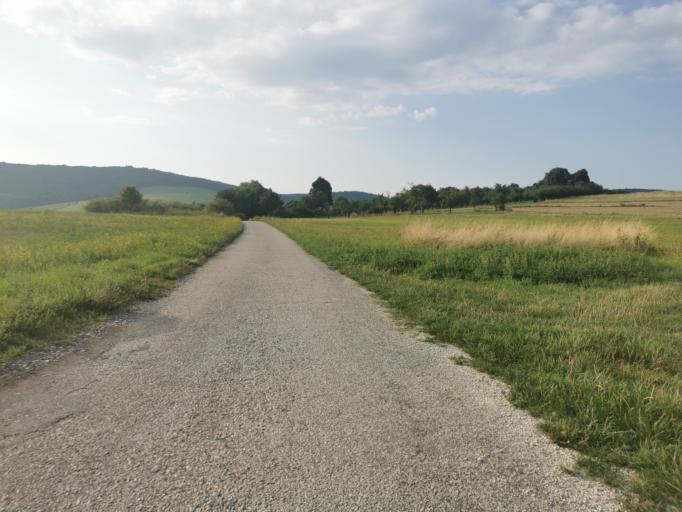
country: SK
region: Trenciansky
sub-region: Okres Myjava
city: Myjava
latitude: 48.7941
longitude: 17.5722
